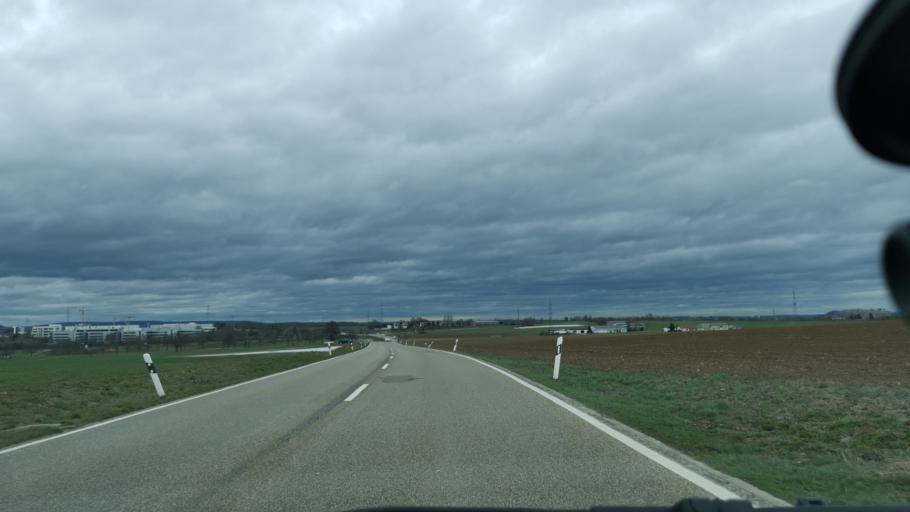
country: DE
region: Baden-Wuerttemberg
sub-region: Regierungsbezirk Stuttgart
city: Schwieberdingen
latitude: 48.8718
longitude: 9.0982
